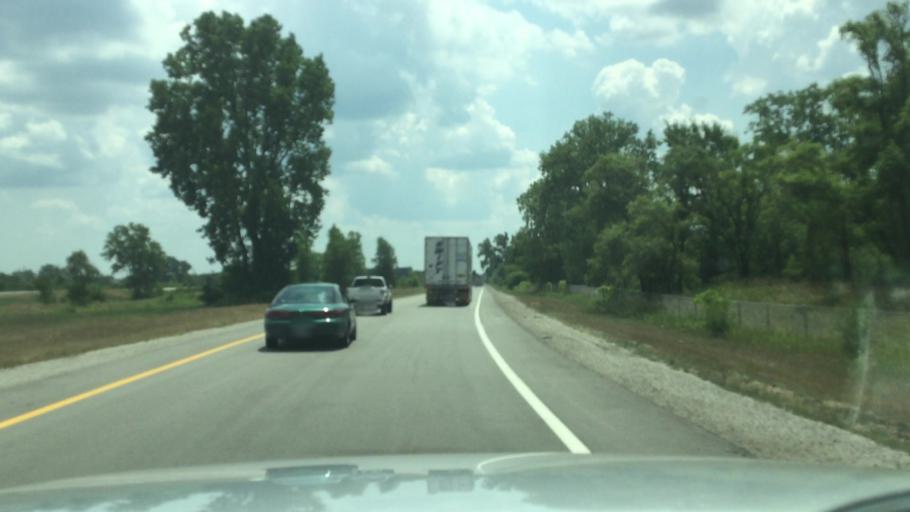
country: US
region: Michigan
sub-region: Washtenaw County
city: Ypsilanti
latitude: 42.2362
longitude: -83.5631
